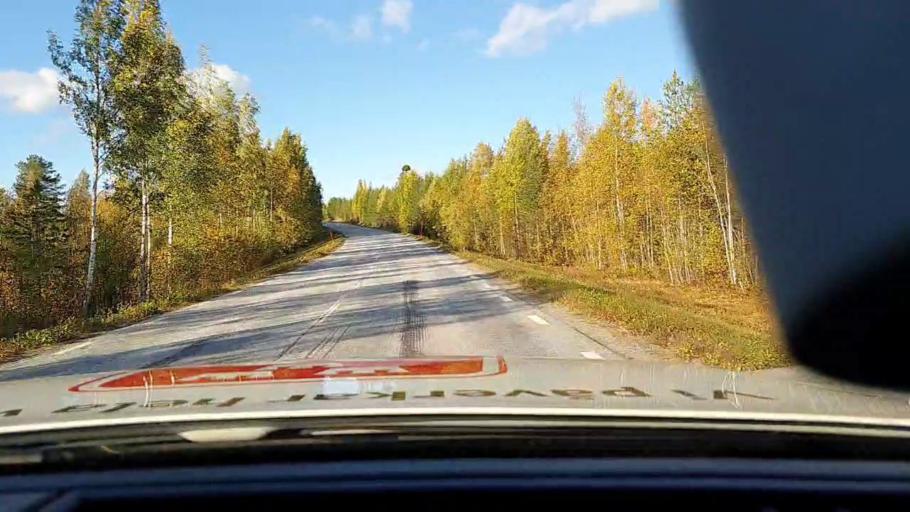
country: SE
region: Norrbotten
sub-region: Pitea Kommun
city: Norrfjarden
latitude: 65.4502
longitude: 21.4568
